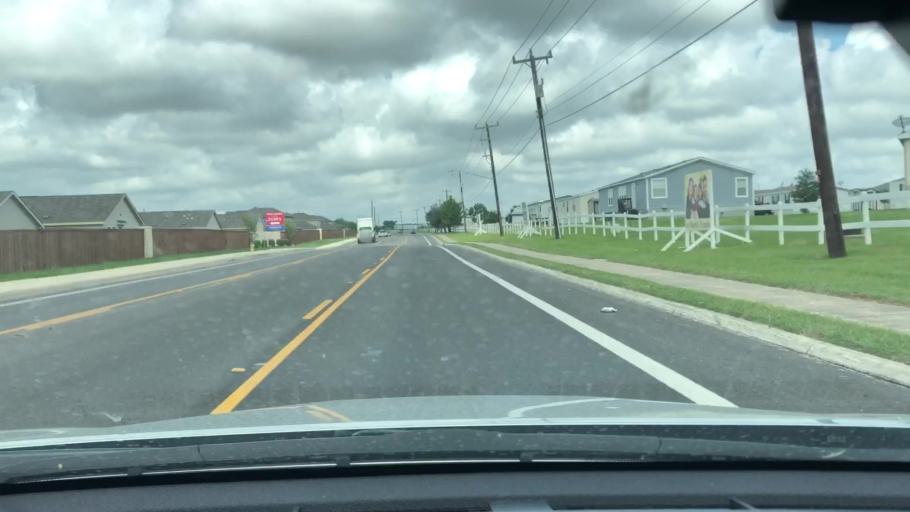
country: US
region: Texas
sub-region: Bexar County
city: Windcrest
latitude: 29.4936
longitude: -98.3594
